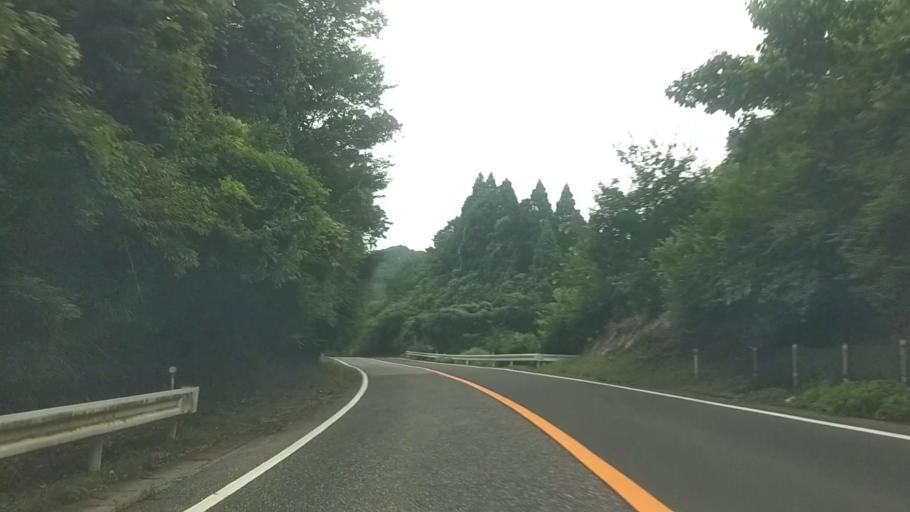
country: JP
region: Chiba
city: Kawaguchi
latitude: 35.2224
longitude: 140.0374
